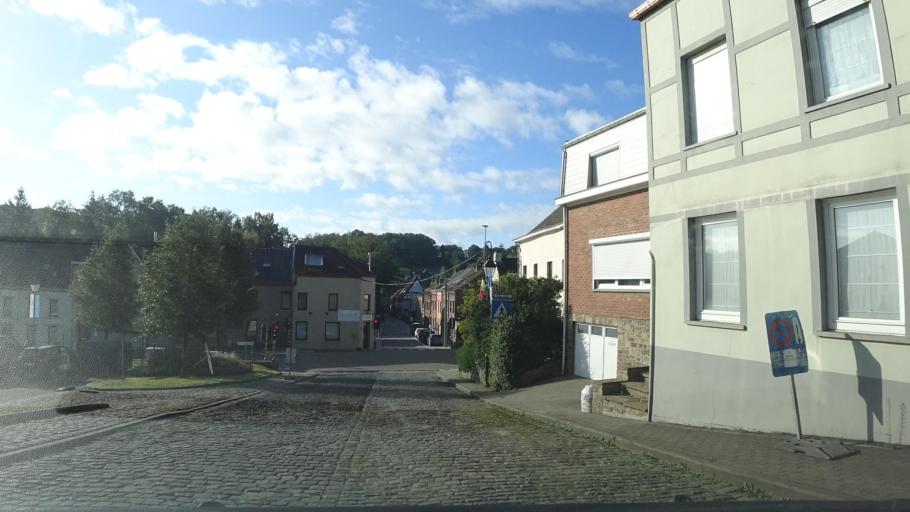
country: BE
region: Wallonia
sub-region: Province du Brabant Wallon
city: Villers-la-Ville
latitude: 50.6165
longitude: 4.5082
